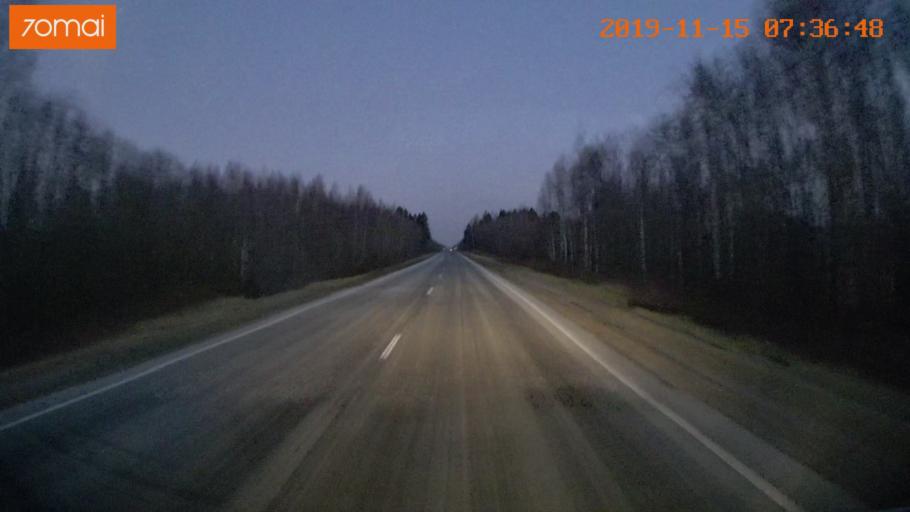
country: RU
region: Vologda
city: Sheksna
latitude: 58.7430
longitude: 38.4287
